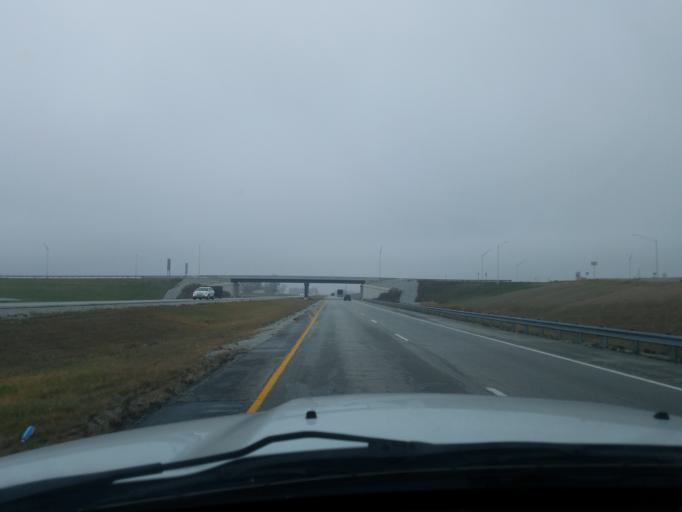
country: US
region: Indiana
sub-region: Tipton County
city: Tipton
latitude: 40.2734
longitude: -86.1269
